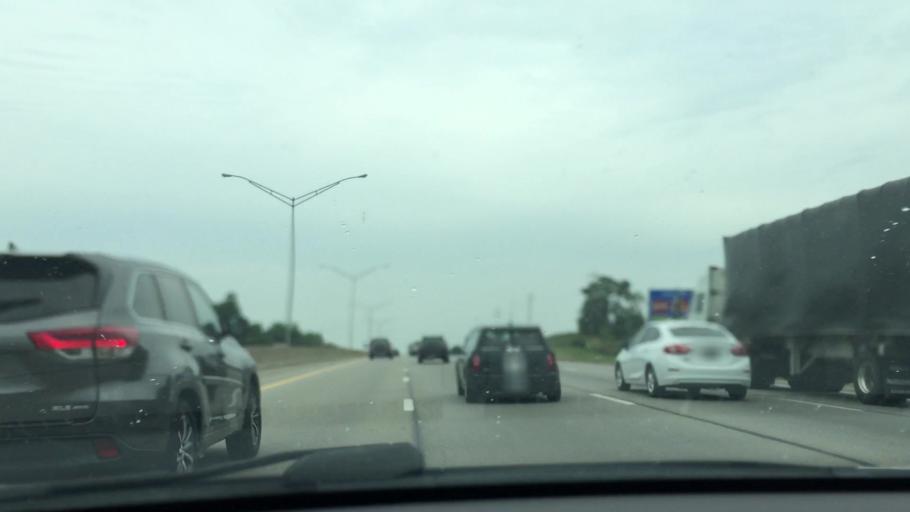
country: US
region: Kentucky
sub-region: Boone County
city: Walton
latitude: 38.9034
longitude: -84.6275
